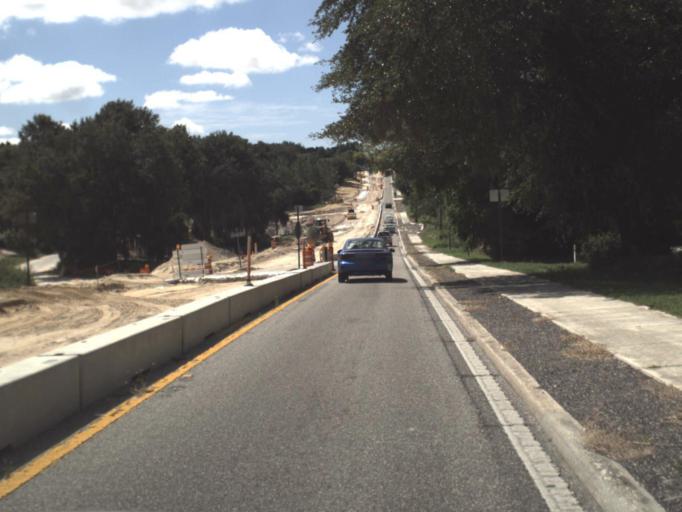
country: US
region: Florida
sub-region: Polk County
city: Haines City
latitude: 28.0938
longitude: -81.6233
